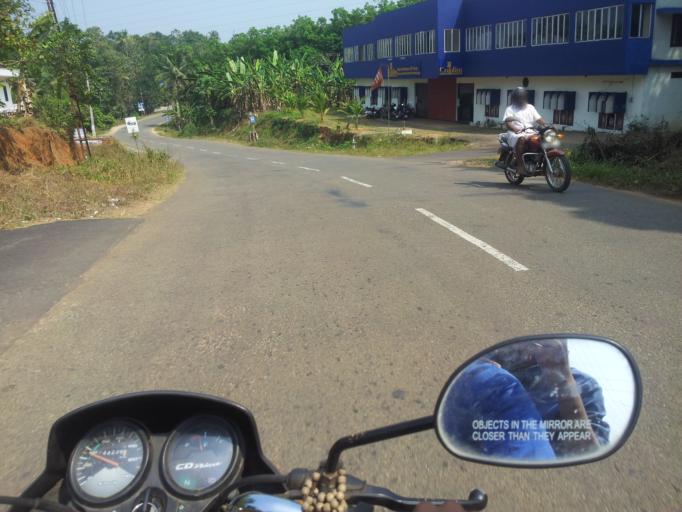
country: IN
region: Kerala
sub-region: Ernakulam
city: Muvattupuzha
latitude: 9.8952
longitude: 76.6995
